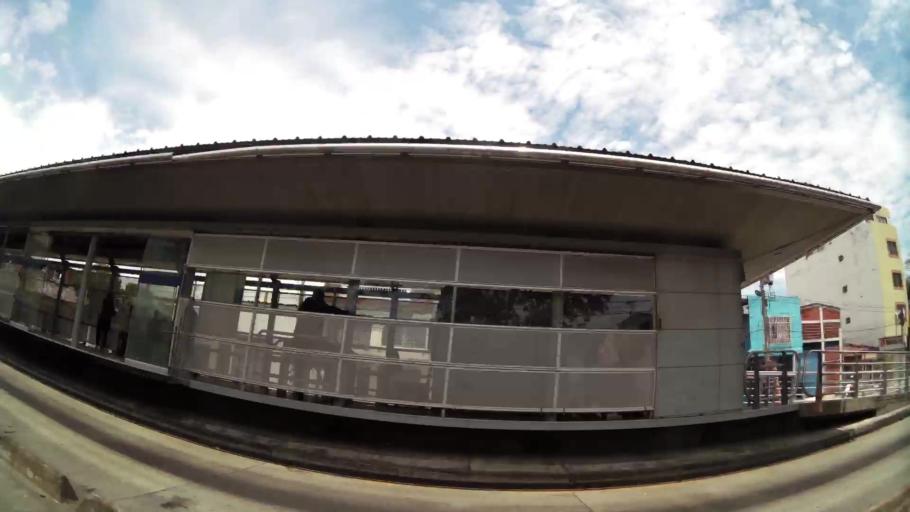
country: CO
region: Valle del Cauca
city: Cali
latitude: 3.4435
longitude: -76.4958
